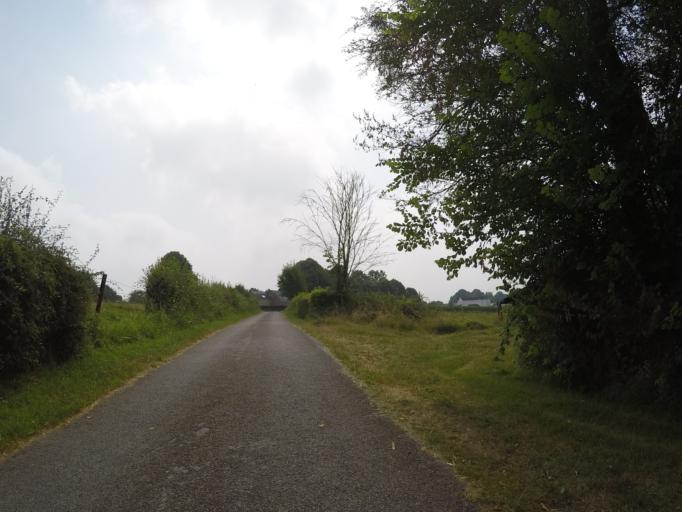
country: BE
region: Wallonia
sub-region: Province de Namur
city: Assesse
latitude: 50.3388
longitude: 4.9698
